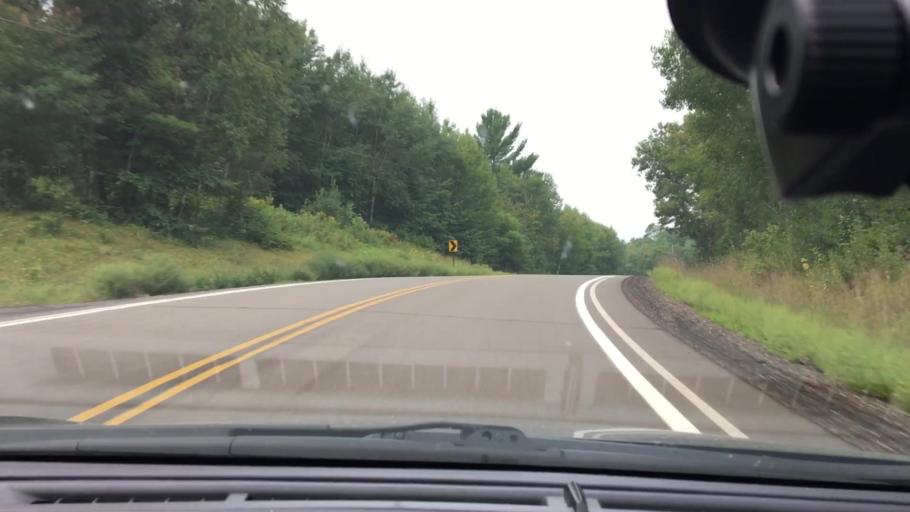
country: US
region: Minnesota
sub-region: Crow Wing County
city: Cross Lake
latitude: 46.6591
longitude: -93.9676
